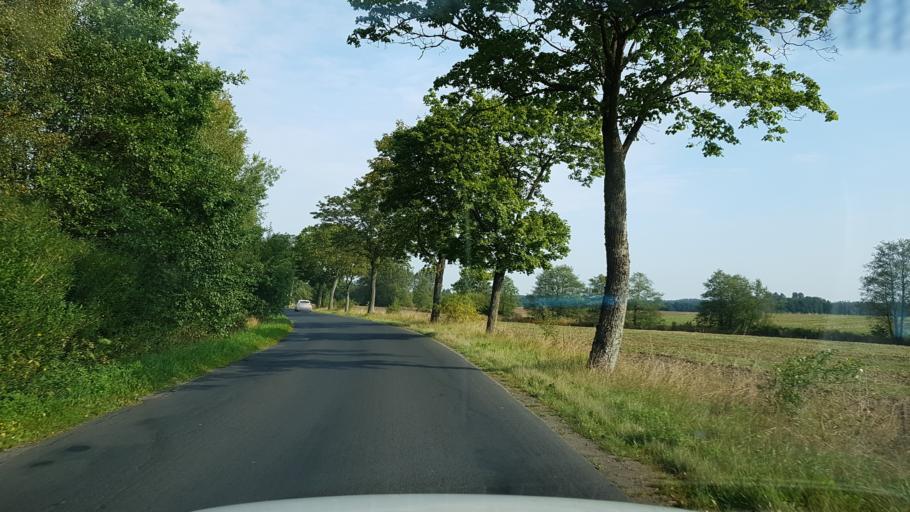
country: PL
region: West Pomeranian Voivodeship
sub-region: Powiat slawienski
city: Slawno
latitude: 54.4286
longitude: 16.6170
